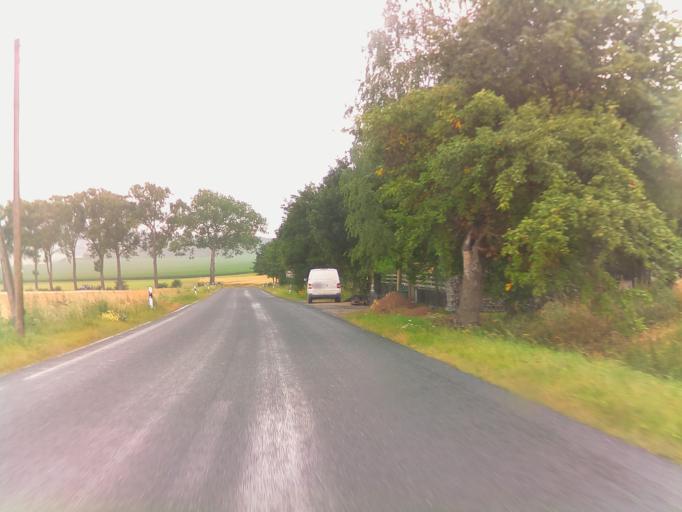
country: DE
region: Thuringia
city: Stadtilm
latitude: 50.7513
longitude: 11.1131
